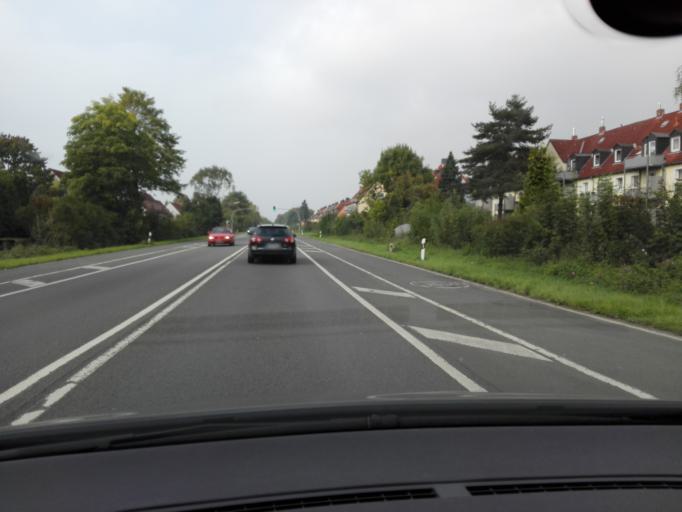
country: DE
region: North Rhine-Westphalia
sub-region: Regierungsbezirk Arnsberg
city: Dortmund
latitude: 51.4765
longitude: 7.4464
